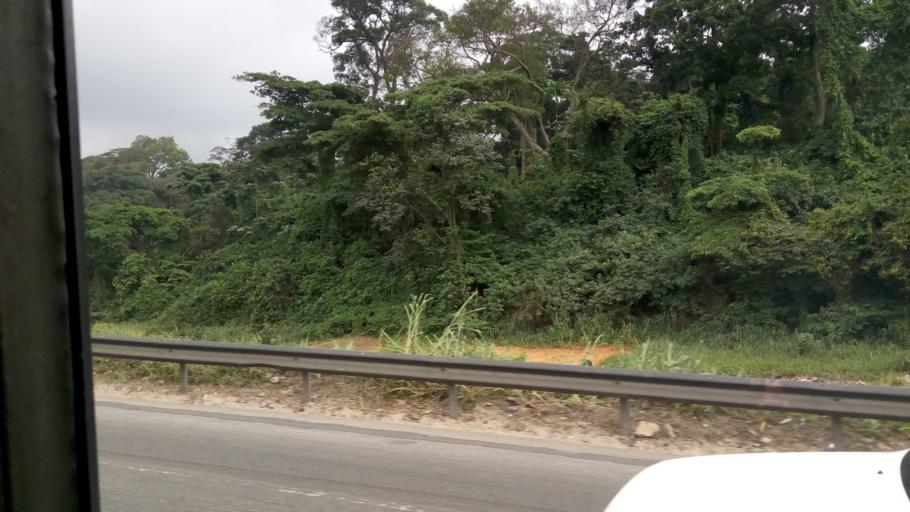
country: CI
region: Lagunes
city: Abidjan
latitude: 5.3588
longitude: -4.0571
